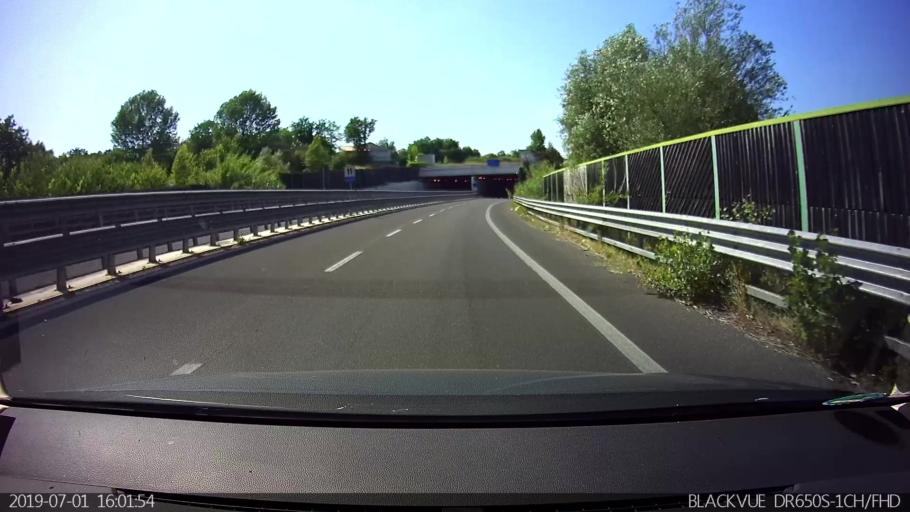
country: IT
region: Latium
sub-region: Provincia di Frosinone
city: Castelmassimo
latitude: 41.6633
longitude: 13.3634
